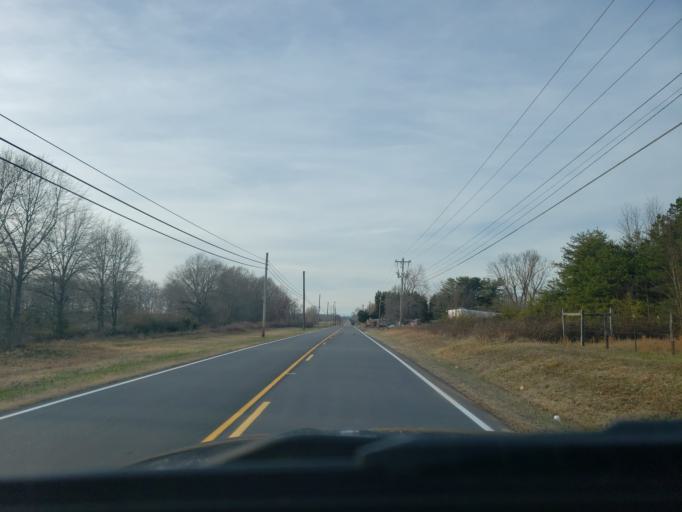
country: US
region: North Carolina
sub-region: Cleveland County
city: Boiling Springs
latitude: 35.3089
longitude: -81.7322
